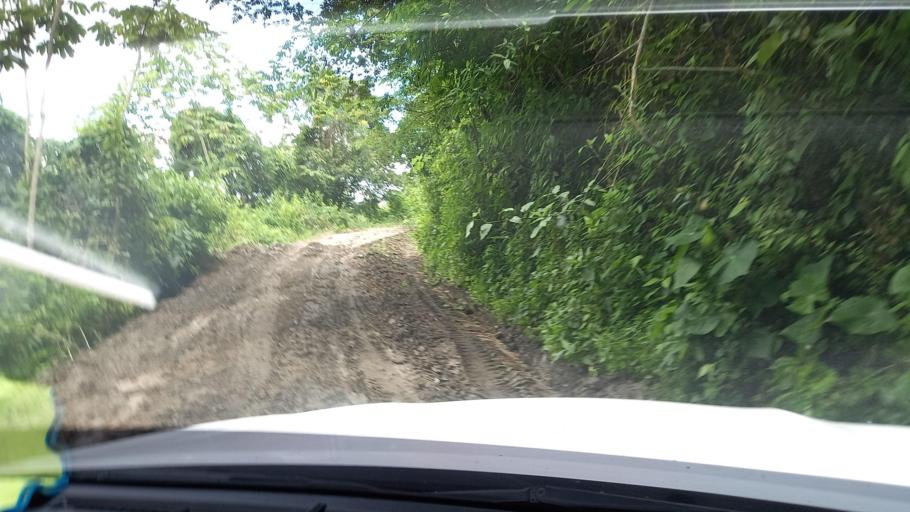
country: NI
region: Nueva Segovia
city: Wiwili
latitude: 13.7250
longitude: -85.7827
